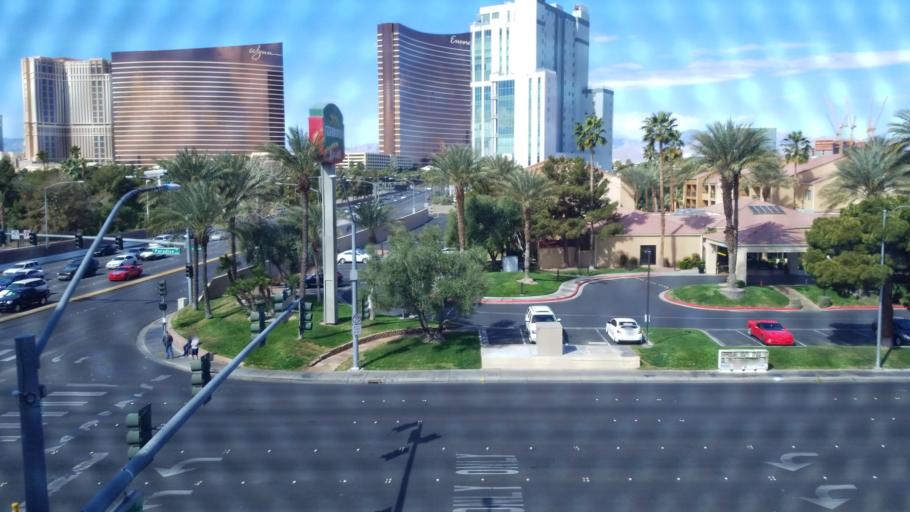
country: US
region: Nevada
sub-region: Clark County
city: Paradise
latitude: 36.1300
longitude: -115.1545
